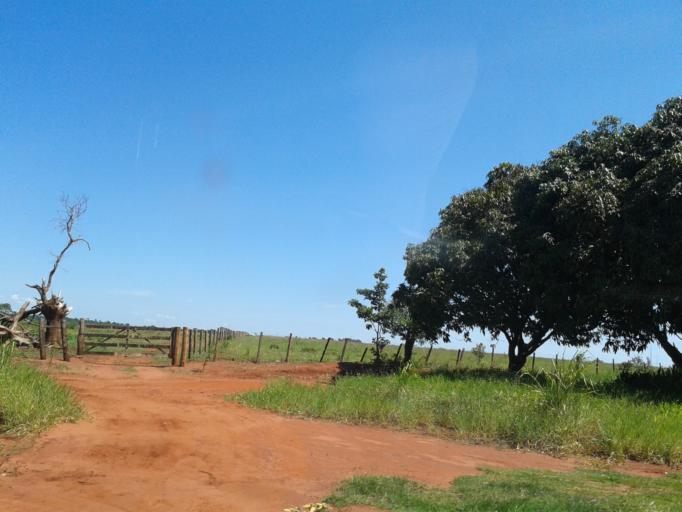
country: BR
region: Minas Gerais
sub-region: Centralina
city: Centralina
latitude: -18.7191
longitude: -49.1430
